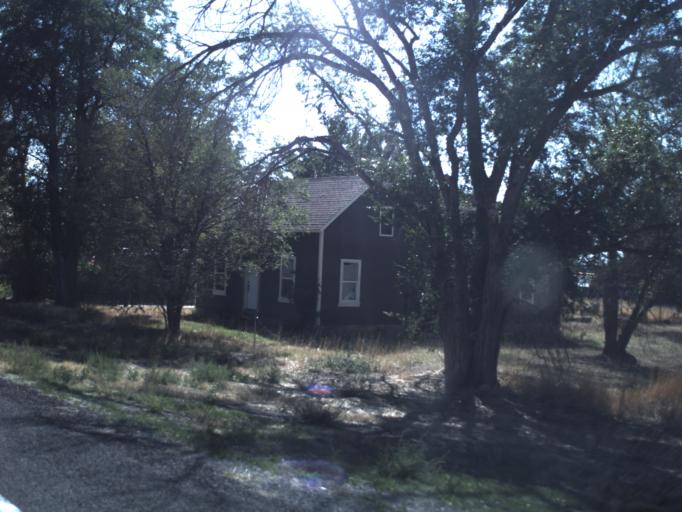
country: US
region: Utah
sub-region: Millard County
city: Fillmore
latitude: 39.1051
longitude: -112.2710
